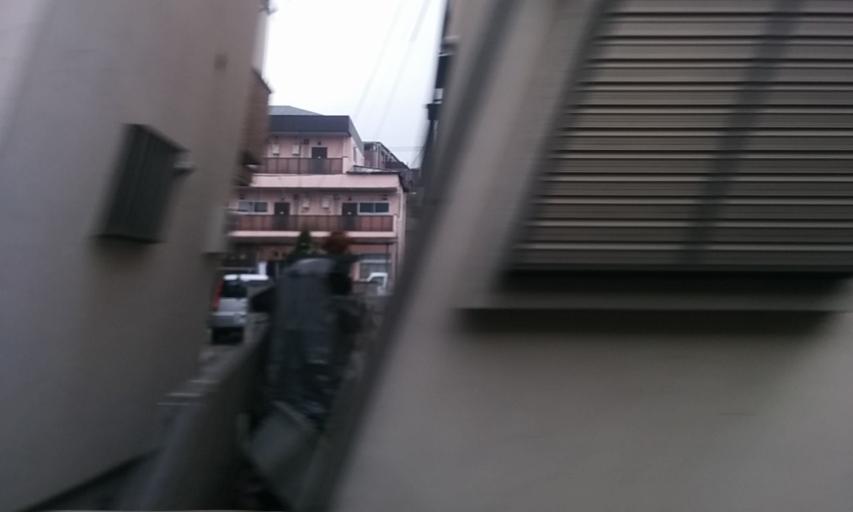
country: JP
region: Tokyo
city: Hino
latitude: 35.6592
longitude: 139.4237
